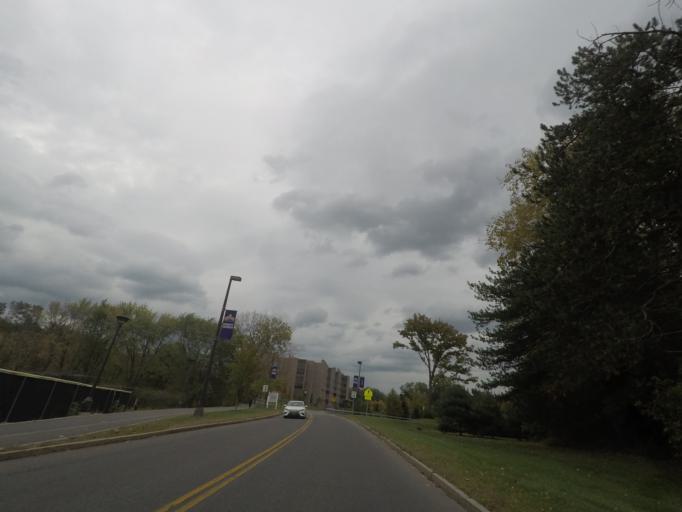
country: US
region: New York
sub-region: Albany County
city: Roessleville
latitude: 42.6779
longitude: -73.8233
